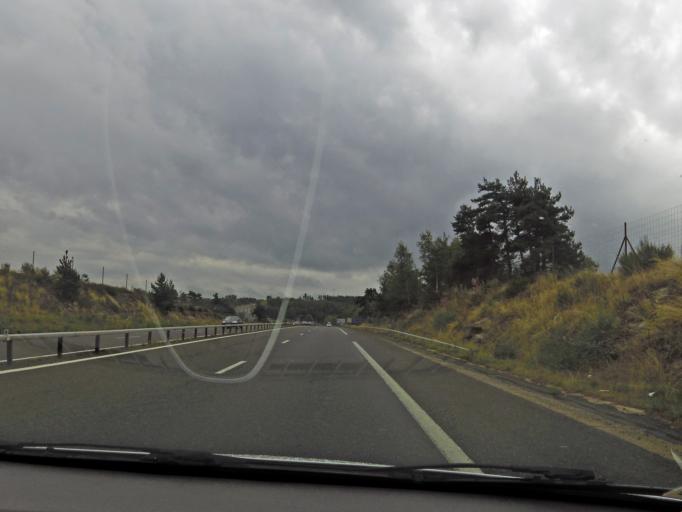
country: FR
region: Languedoc-Roussillon
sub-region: Departement de la Lozere
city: Le Malzieu-Ville
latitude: 44.8850
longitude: 3.2370
